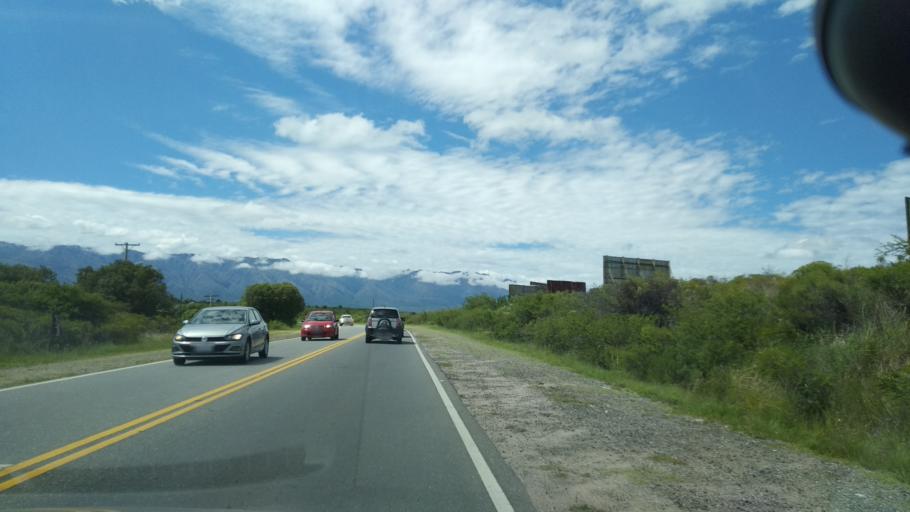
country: AR
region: Cordoba
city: Mina Clavero
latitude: -31.7546
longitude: -64.9761
